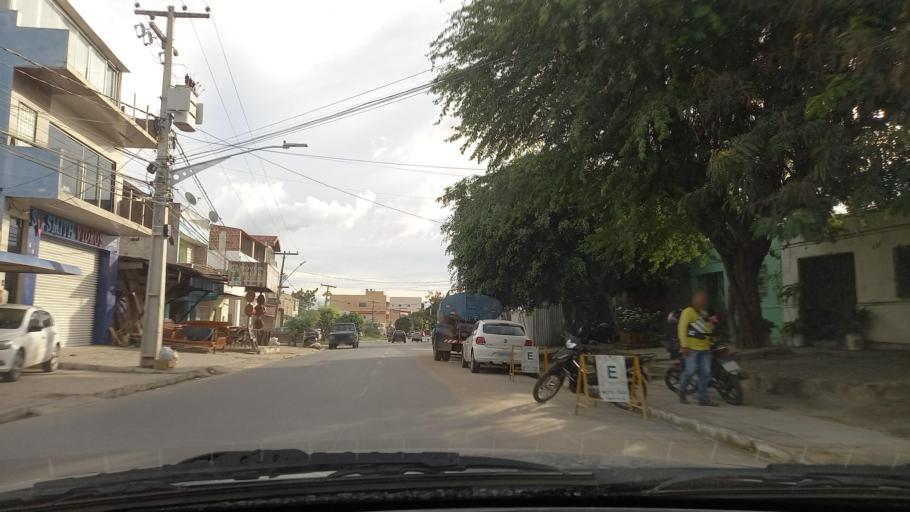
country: BR
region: Pernambuco
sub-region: Gravata
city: Gravata
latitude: -8.1959
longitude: -35.5533
